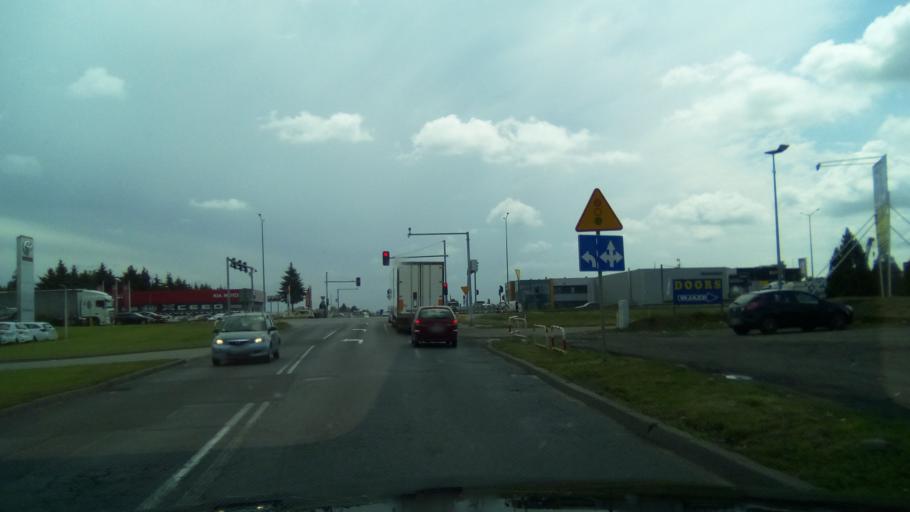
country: PL
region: Greater Poland Voivodeship
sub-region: Powiat poznanski
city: Komorniki
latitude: 52.3463
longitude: 16.8271
